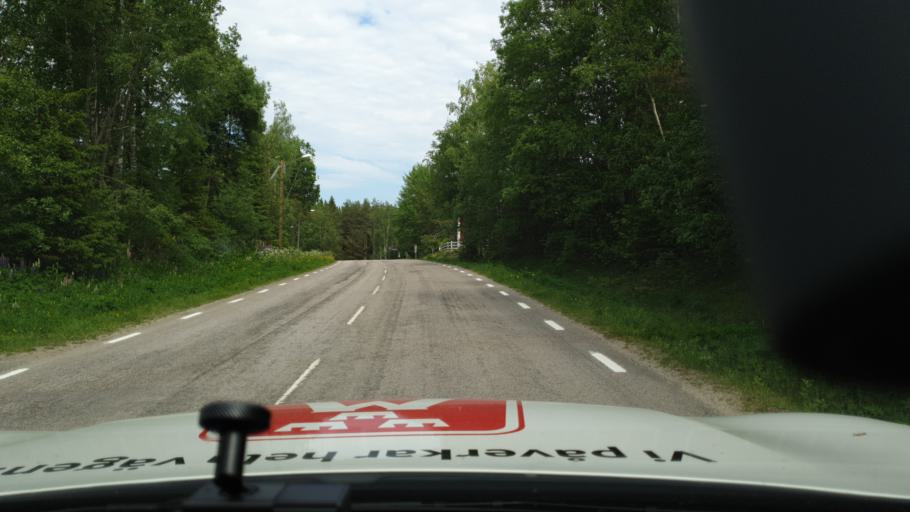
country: SE
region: Vaesterbotten
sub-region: Umea Kommun
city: Hoernefors
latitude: 63.5680
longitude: 19.8212
